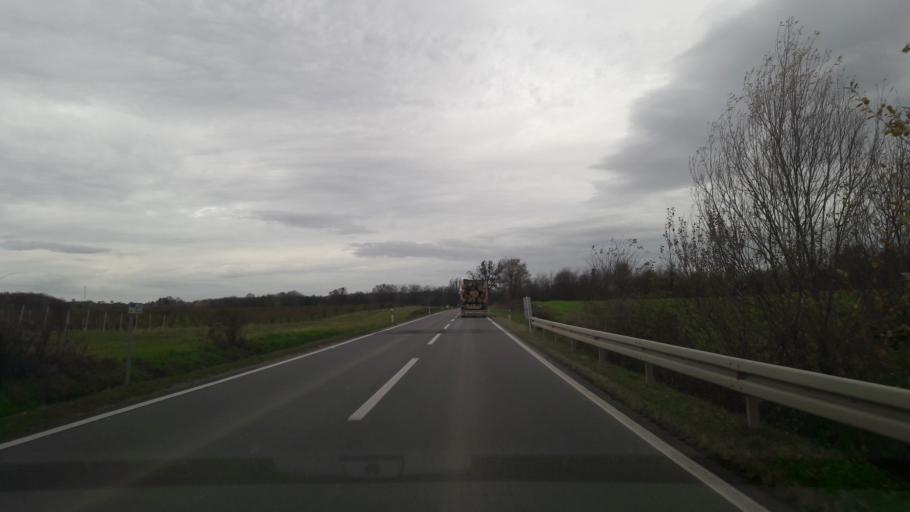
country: HR
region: Virovitick-Podravska
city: Orahovica
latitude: 45.5398
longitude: 17.9254
